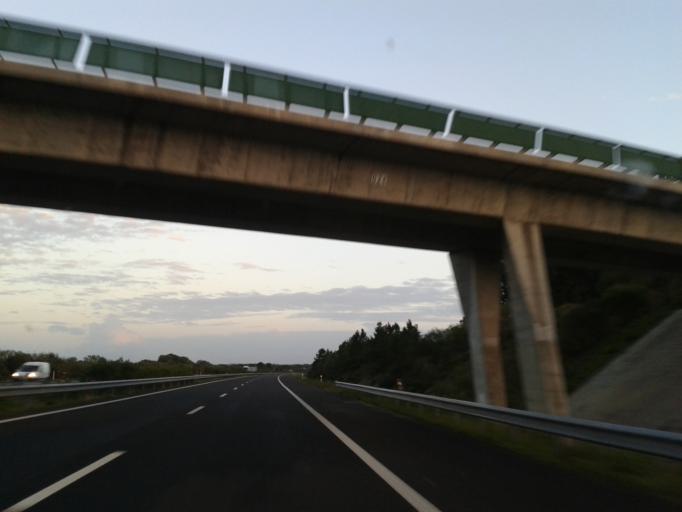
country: PT
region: Santarem
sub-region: Benavente
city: Poceirao
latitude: 38.7178
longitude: -8.6579
